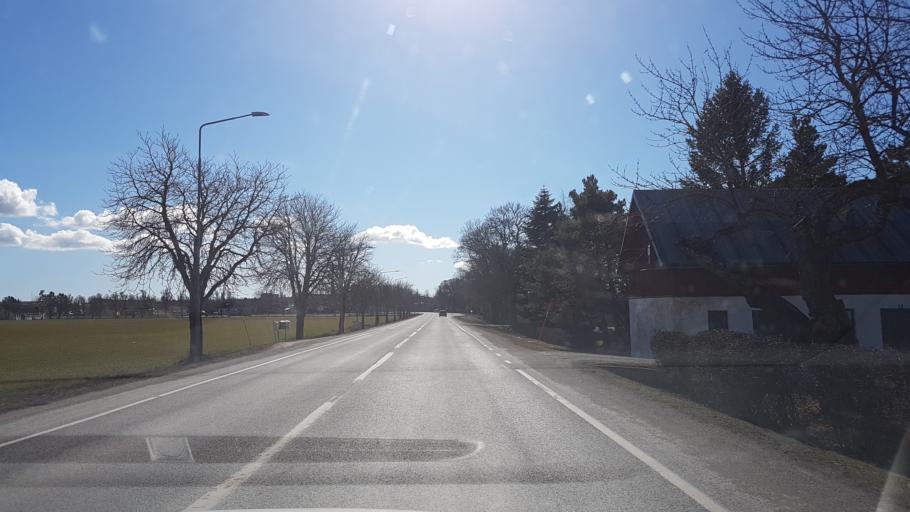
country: SE
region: Gotland
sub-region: Gotland
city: Visby
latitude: 57.5145
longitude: 18.4450
